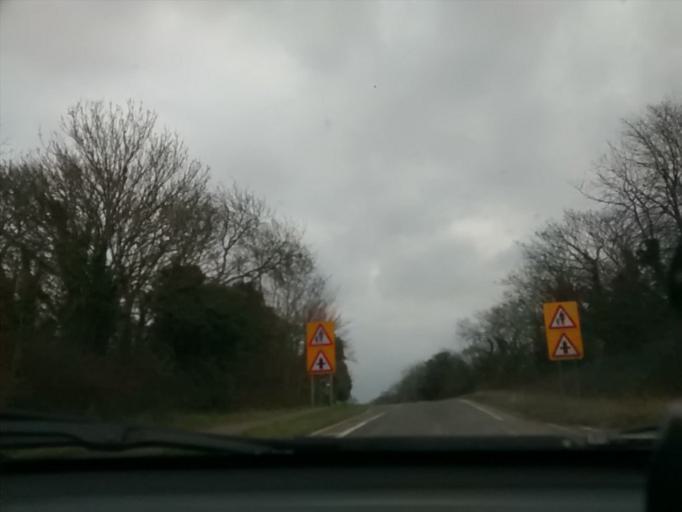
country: GB
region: England
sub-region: Cambridgeshire
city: Sawston
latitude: 52.1583
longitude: 0.1766
